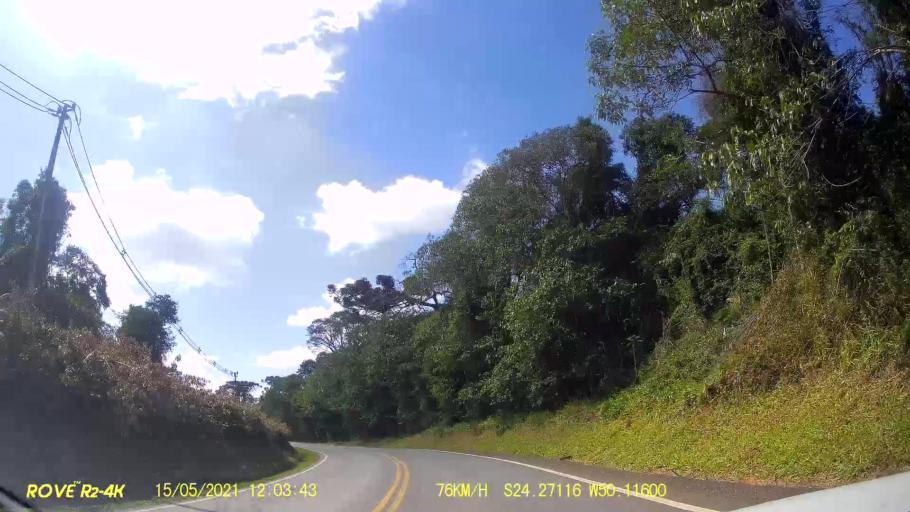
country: BR
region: Parana
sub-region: Pirai Do Sul
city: Pirai do Sul
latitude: -24.2711
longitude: -50.1160
